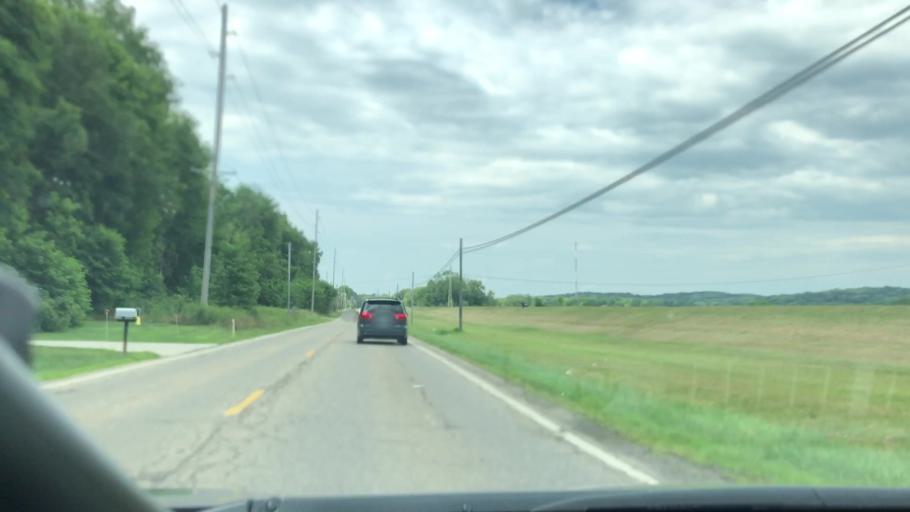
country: US
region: Ohio
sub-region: Summit County
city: New Franklin
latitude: 40.9420
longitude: -81.5344
